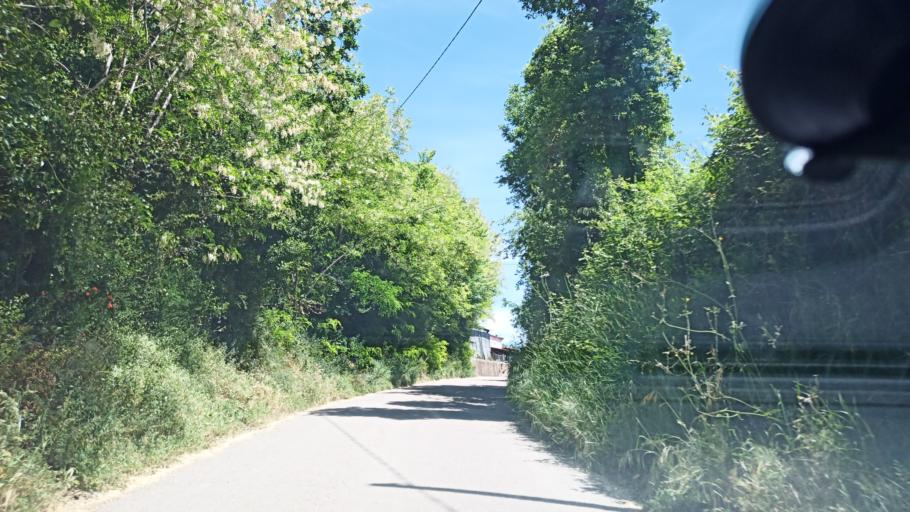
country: IT
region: Latium
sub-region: Provincia di Rieti
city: Torri in Sabina
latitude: 42.3497
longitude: 12.6212
